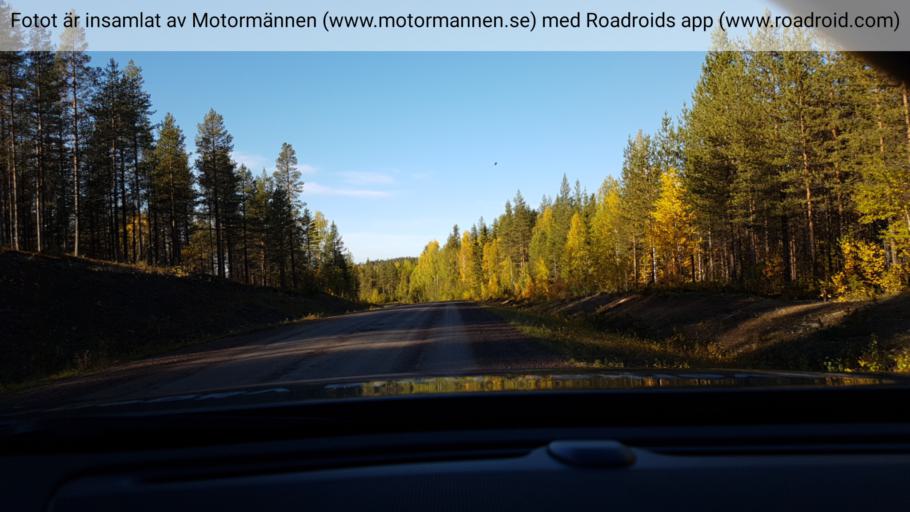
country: SE
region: Norrbotten
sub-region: Alvsbyns Kommun
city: AElvsbyn
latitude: 66.2584
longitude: 20.9507
